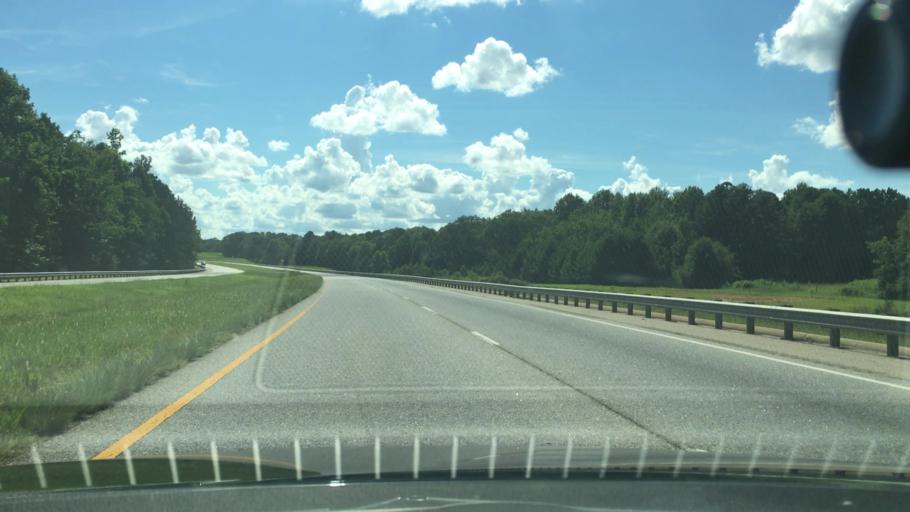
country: US
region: Georgia
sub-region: Spalding County
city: East Griffin
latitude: 33.2382
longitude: -84.2087
